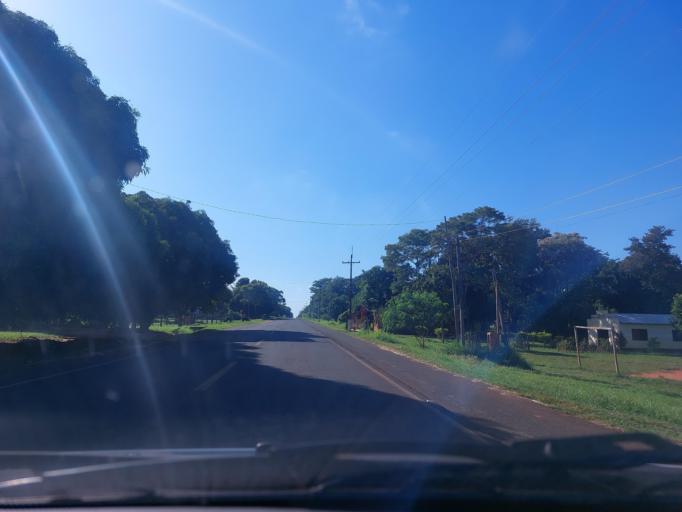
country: PY
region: San Pedro
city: Guayaybi
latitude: -24.5317
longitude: -56.4727
